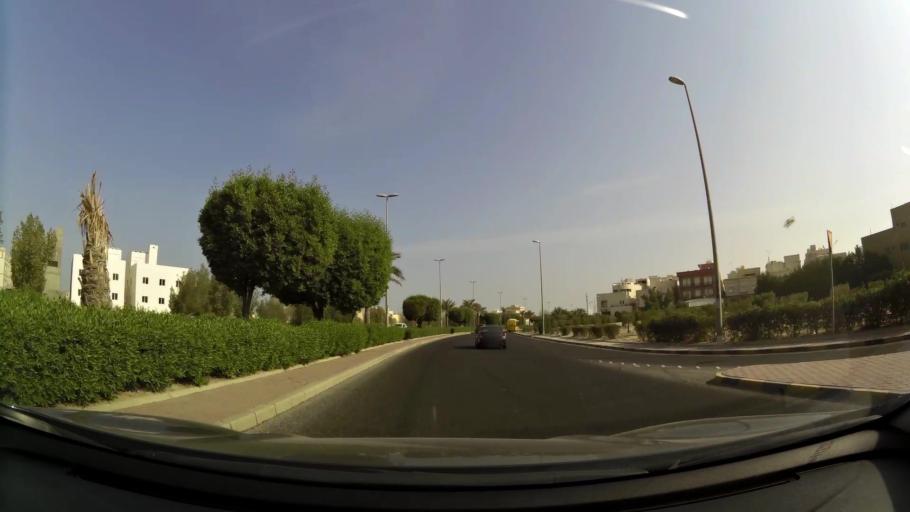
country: KW
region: Mubarak al Kabir
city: Mubarak al Kabir
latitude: 29.1949
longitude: 48.0956
